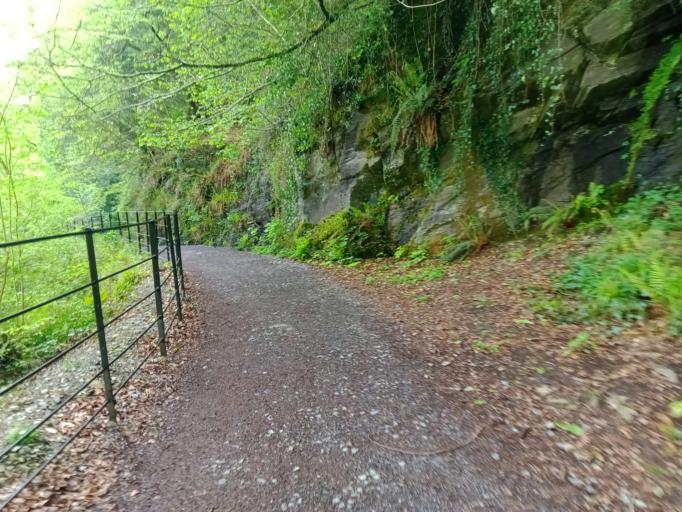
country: IE
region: Leinster
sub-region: Kilkenny
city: Thomastown
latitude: 52.4826
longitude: -7.0643
